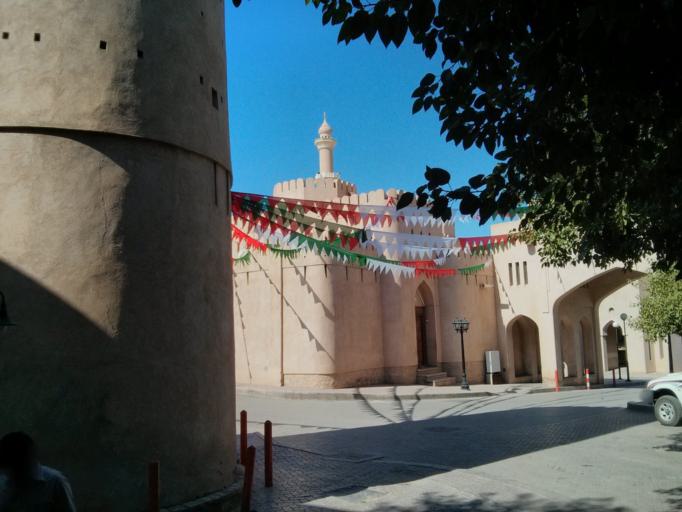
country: OM
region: Muhafazat ad Dakhiliyah
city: Nizwa
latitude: 22.9329
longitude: 57.5314
